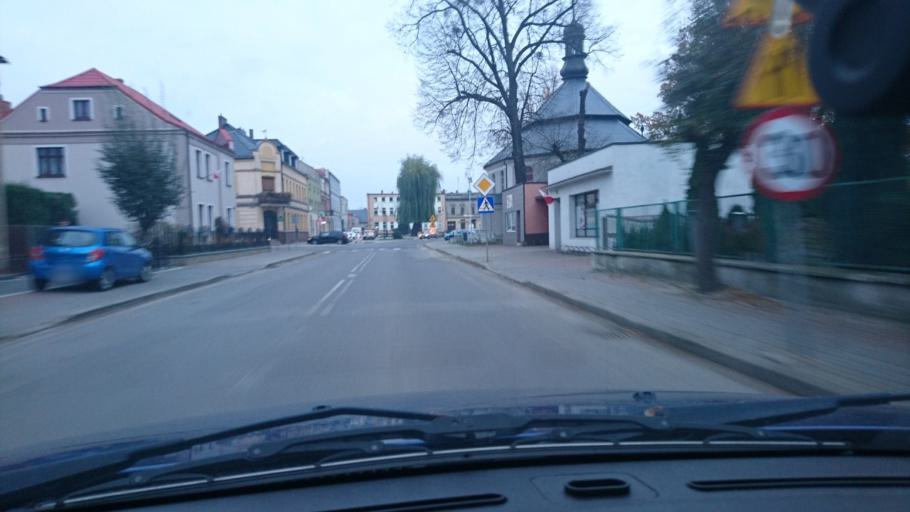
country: PL
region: Greater Poland Voivodeship
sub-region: Powiat ostrowski
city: Odolanow
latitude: 51.5741
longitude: 17.6707
